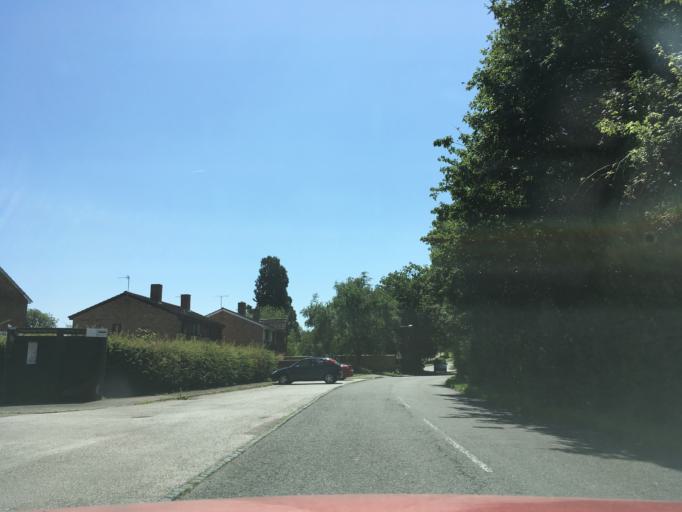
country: GB
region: England
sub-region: Milton Keynes
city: Simpson
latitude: 52.0279
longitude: -0.7223
